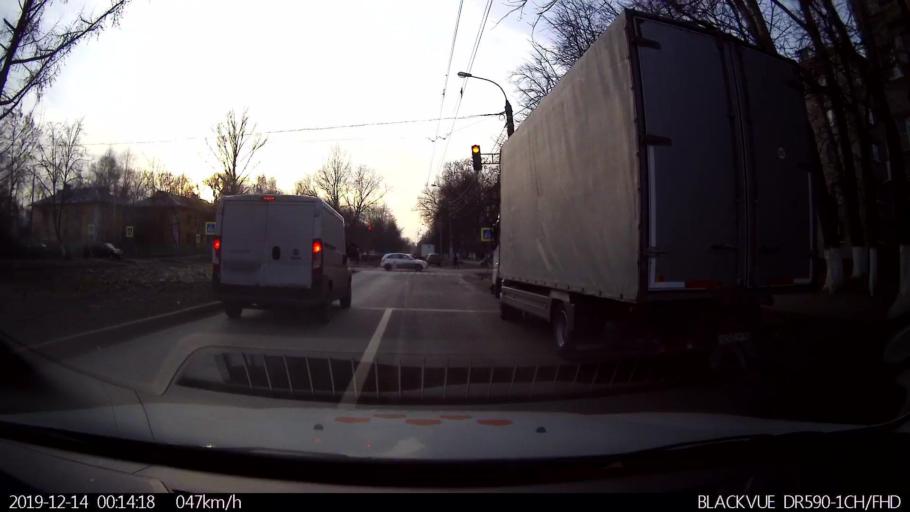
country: RU
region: Nizjnij Novgorod
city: Burevestnik
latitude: 56.2328
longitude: 43.8552
